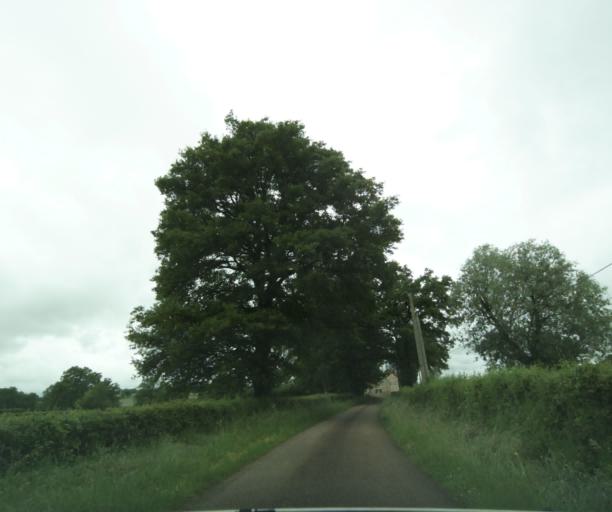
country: FR
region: Bourgogne
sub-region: Departement de Saone-et-Loire
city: Charolles
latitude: 46.4653
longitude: 4.3694
